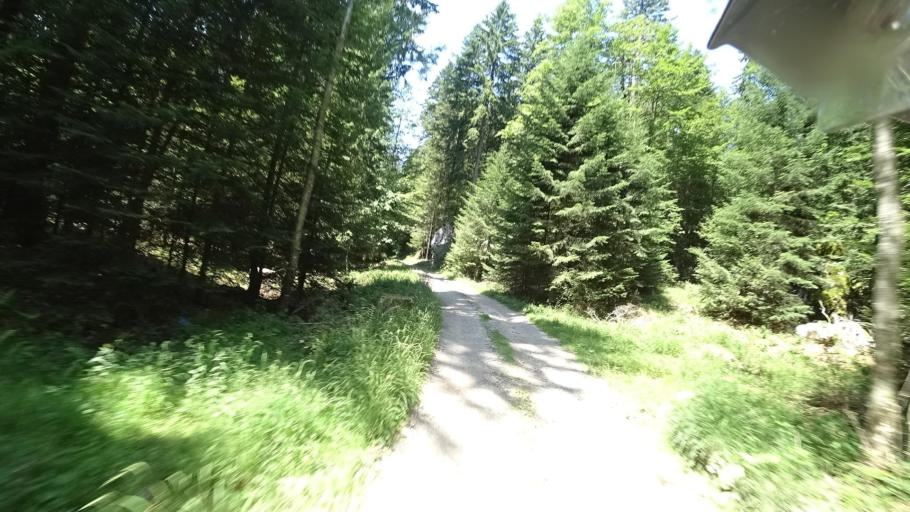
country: HR
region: Primorsko-Goranska
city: Bribir
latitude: 45.2614
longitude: 14.8928
